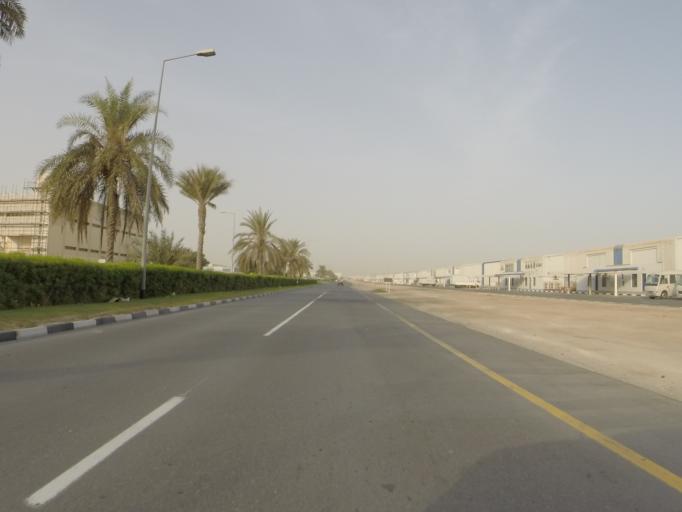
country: AE
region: Dubai
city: Dubai
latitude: 24.9655
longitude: 55.0708
